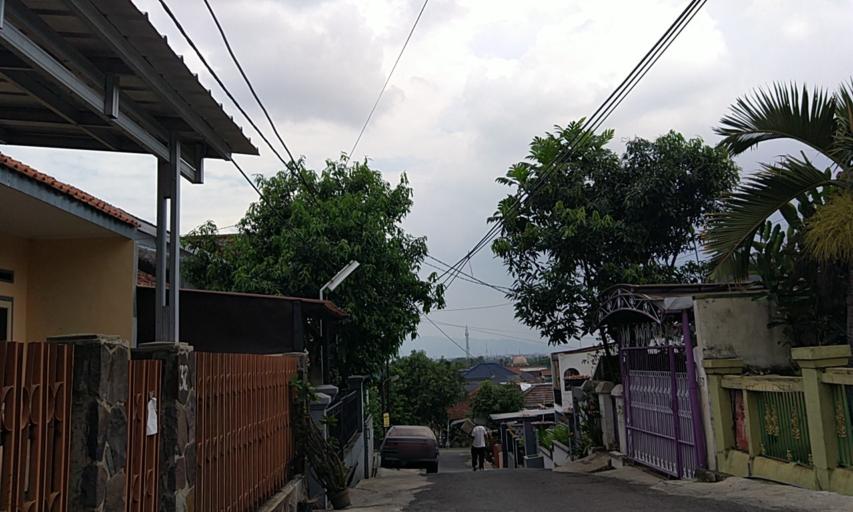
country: ID
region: West Java
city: Cileunyi
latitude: -6.9029
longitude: 107.6929
